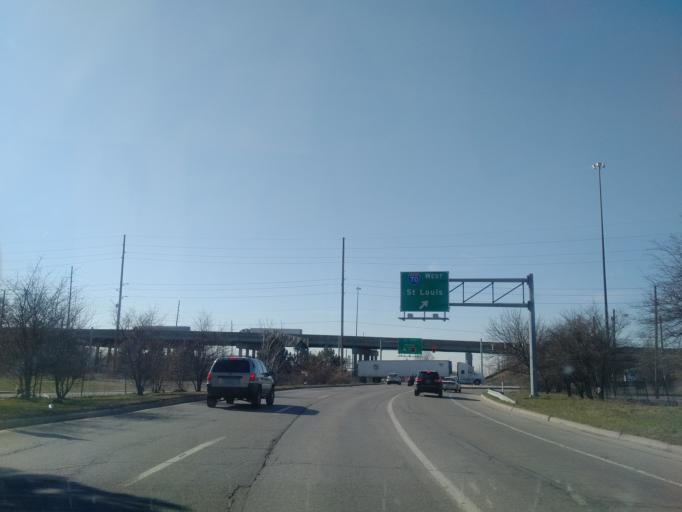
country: US
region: Indiana
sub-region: Marion County
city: Indianapolis
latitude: 39.7552
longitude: -86.1670
